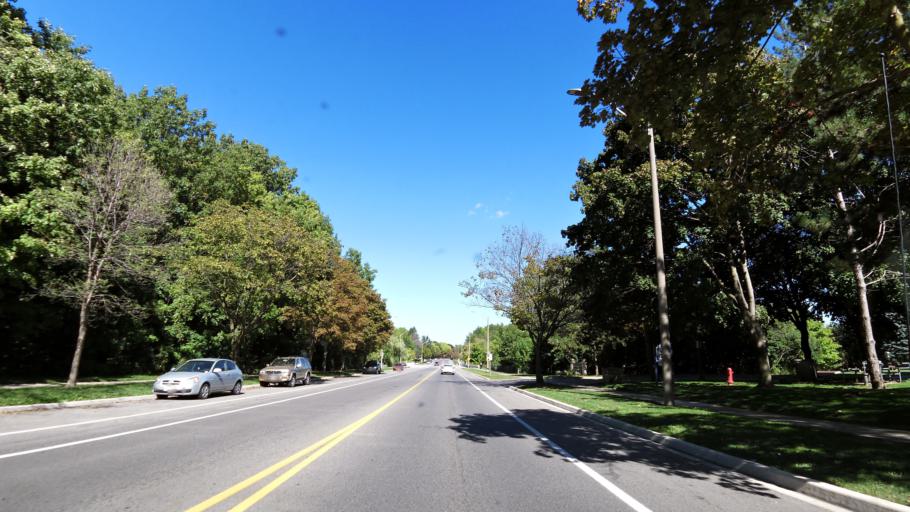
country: CA
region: Ontario
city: Mississauga
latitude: 43.5952
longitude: -79.6293
